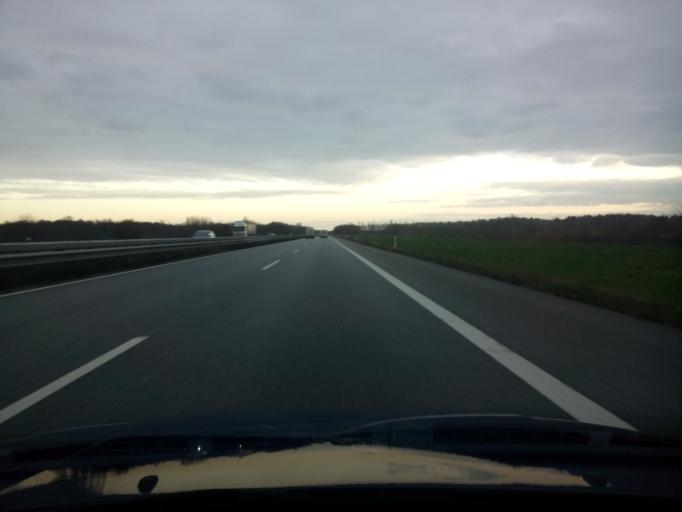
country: DE
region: Lower Saxony
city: Uthlede
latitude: 53.3458
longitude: 8.6015
